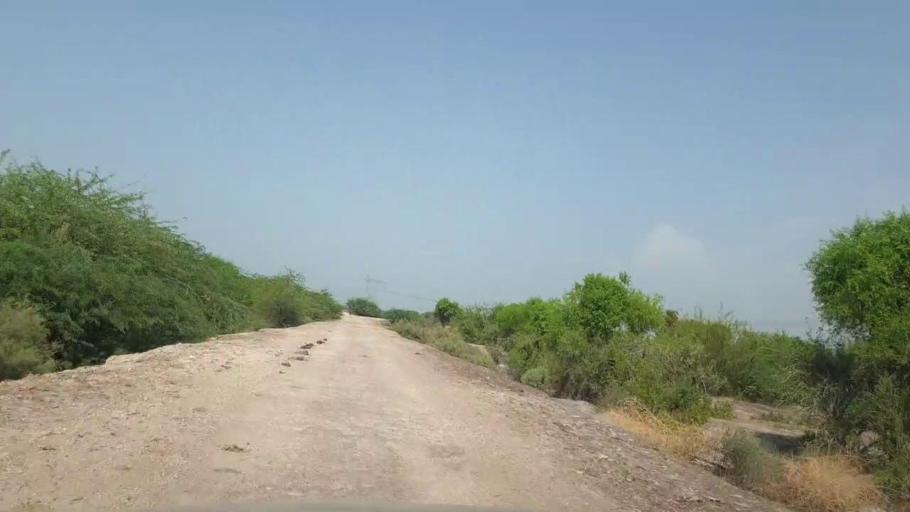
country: PK
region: Sindh
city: Pano Aqil
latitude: 27.7608
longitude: 69.1903
